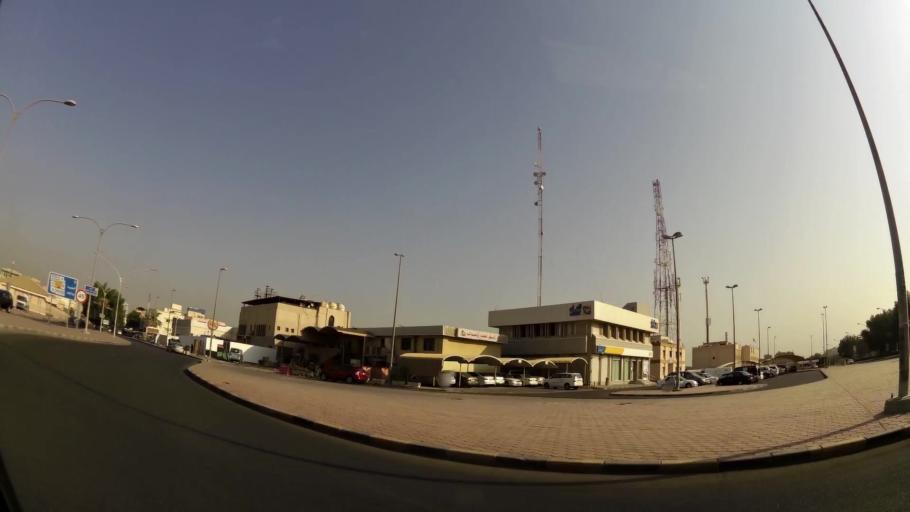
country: KW
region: Muhafazat Hawalli
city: Hawalli
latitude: 29.3162
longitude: 48.0342
